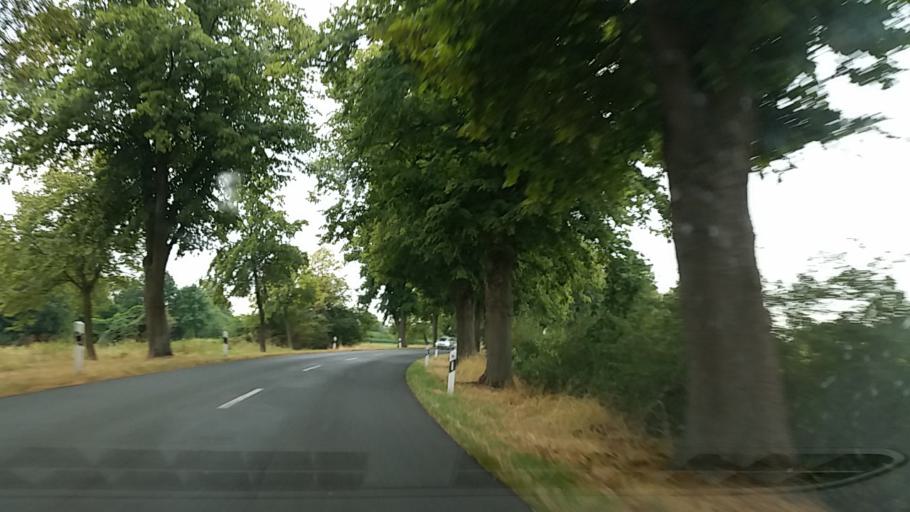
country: DE
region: Lower Saxony
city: Gilten
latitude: 52.7005
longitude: 9.5982
